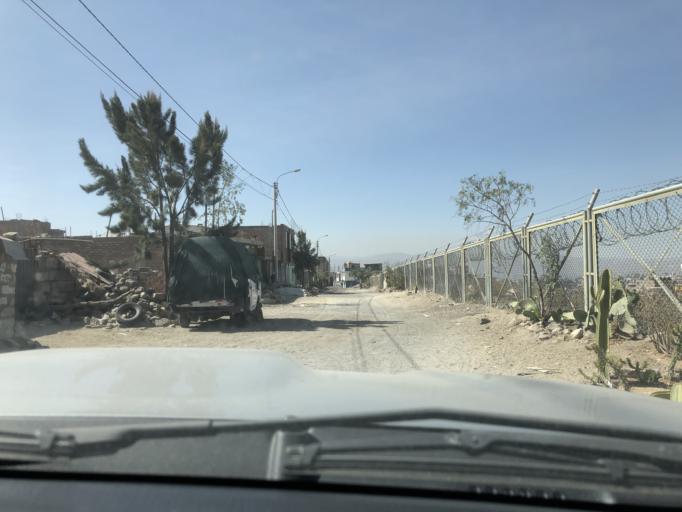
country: PE
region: Arequipa
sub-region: Provincia de Arequipa
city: Arequipa
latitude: -16.3418
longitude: -71.5524
